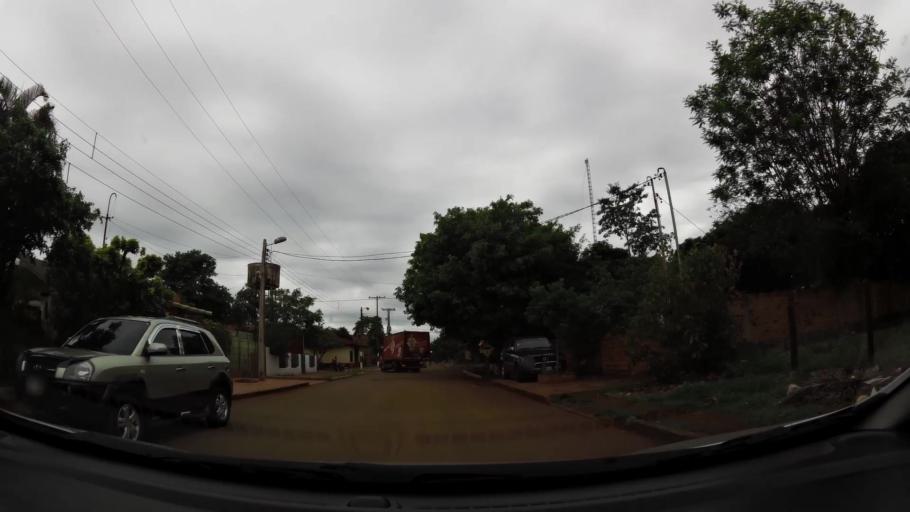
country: PY
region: Alto Parana
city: Ciudad del Este
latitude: -25.4352
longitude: -54.6452
